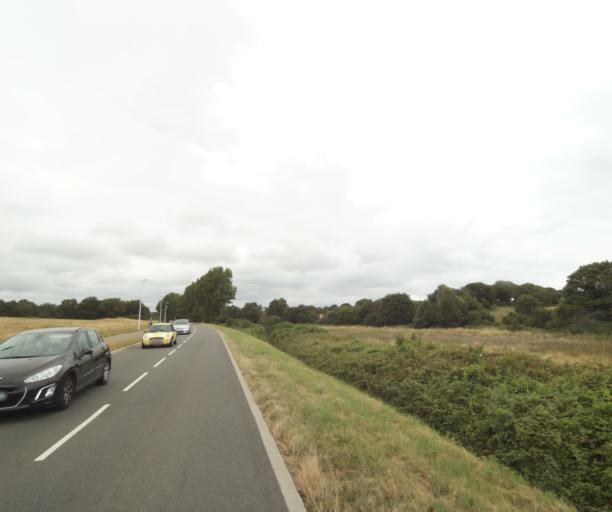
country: FR
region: Pays de la Loire
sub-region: Departement de la Vendee
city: Chateau-d'Olonne
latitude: 46.4946
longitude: -1.7437
